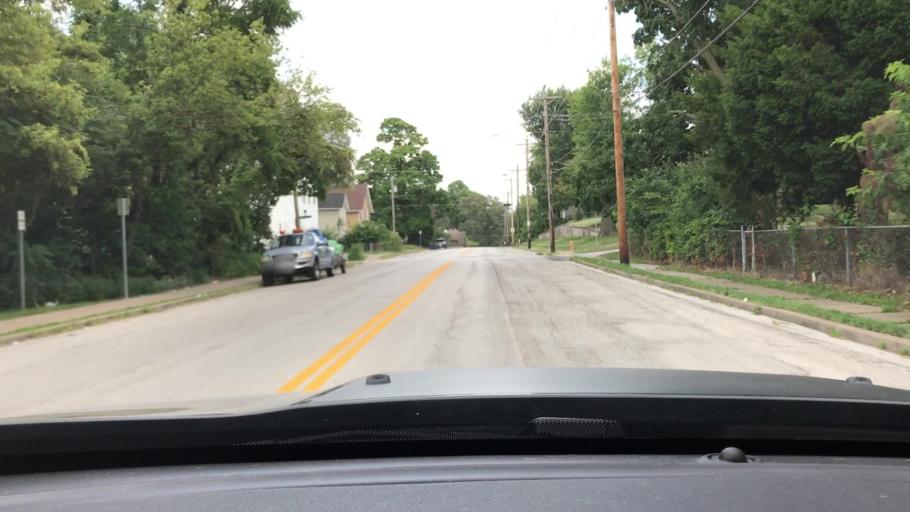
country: US
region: Iowa
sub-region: Scott County
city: Davenport
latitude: 41.5323
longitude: -90.5545
